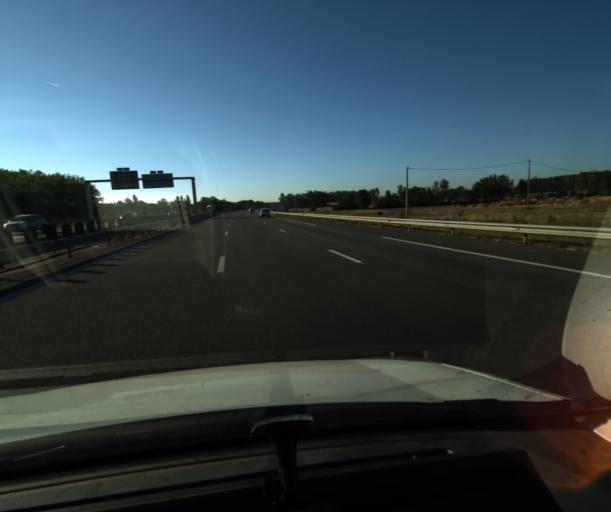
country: FR
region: Midi-Pyrenees
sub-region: Departement du Tarn-et-Garonne
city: Campsas
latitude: 43.9245
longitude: 1.3131
